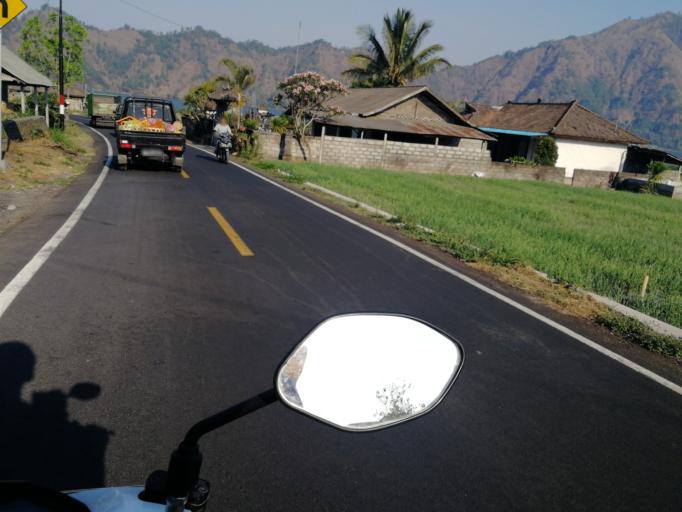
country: ID
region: Bali
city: Banjar Trunyan
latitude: -8.2403
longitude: 115.4059
